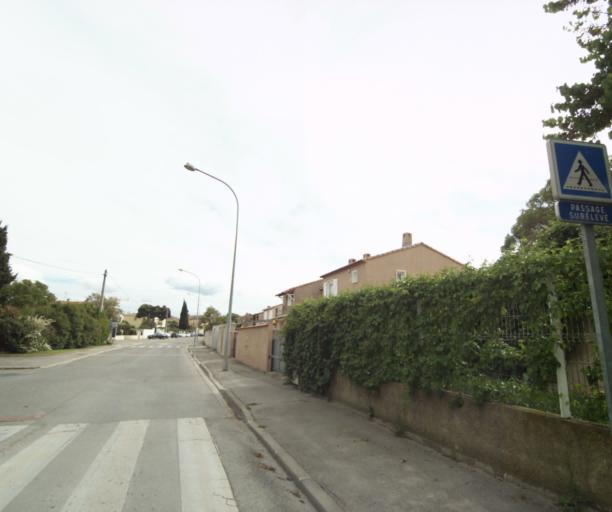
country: FR
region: Provence-Alpes-Cote d'Azur
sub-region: Departement des Bouches-du-Rhone
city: Rognac
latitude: 43.4898
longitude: 5.2223
